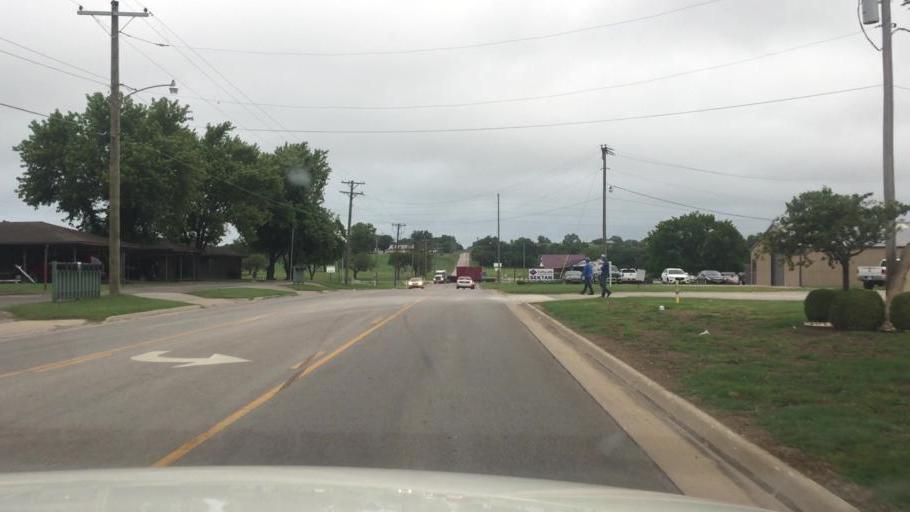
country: US
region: Kansas
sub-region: Montgomery County
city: Coffeyville
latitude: 37.0487
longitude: -95.6473
